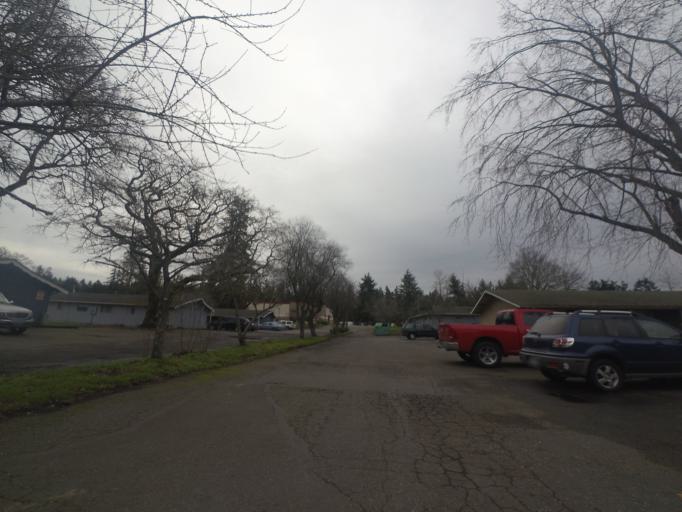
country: US
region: Washington
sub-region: Pierce County
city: McChord Air Force Base
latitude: 47.1221
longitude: -122.5314
